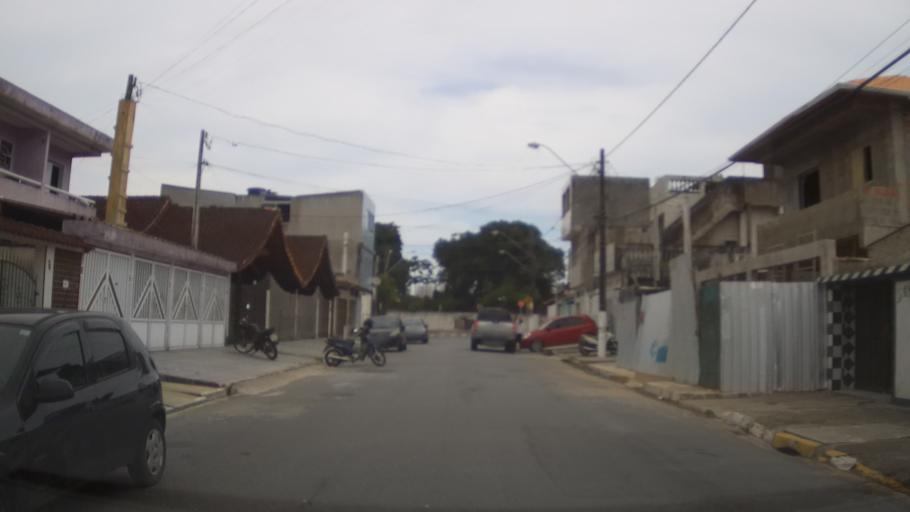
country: BR
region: Sao Paulo
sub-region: Praia Grande
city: Praia Grande
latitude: -24.0080
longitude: -46.4538
